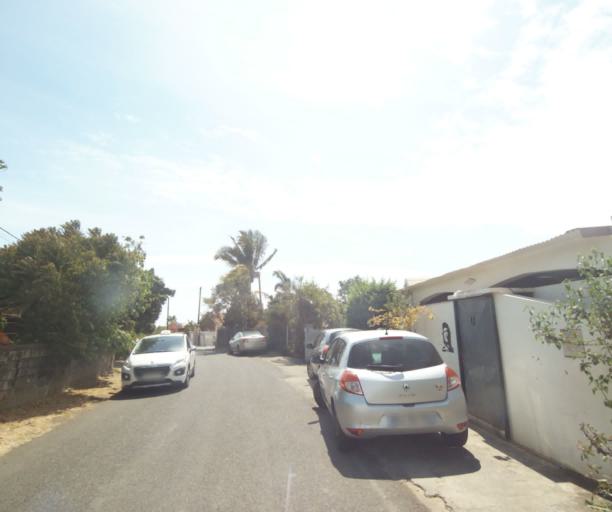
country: RE
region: Reunion
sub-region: Reunion
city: Saint-Paul
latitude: -21.0586
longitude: 55.2602
